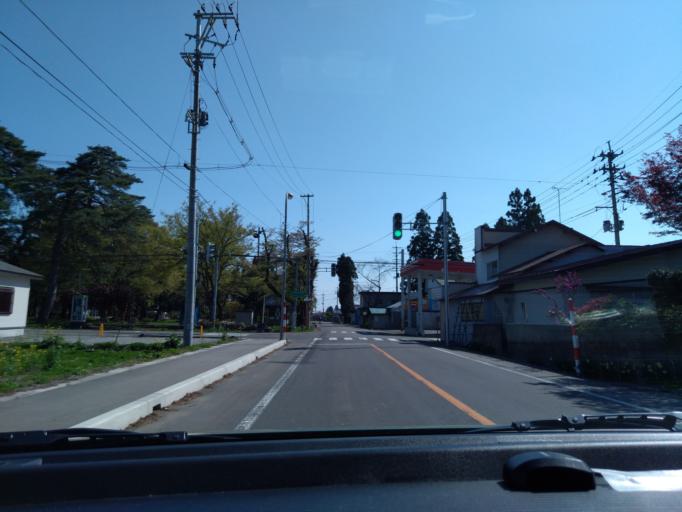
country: JP
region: Akita
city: Omagari
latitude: 39.4735
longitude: 140.5854
